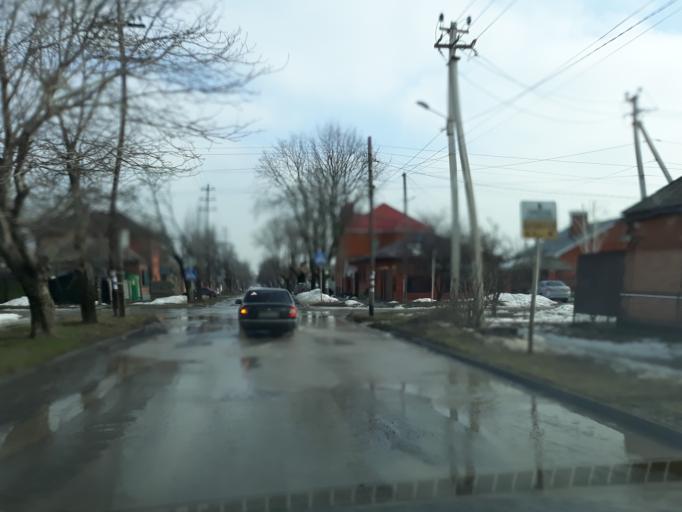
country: RU
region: Rostov
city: Taganrog
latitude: 47.2169
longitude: 38.8949
